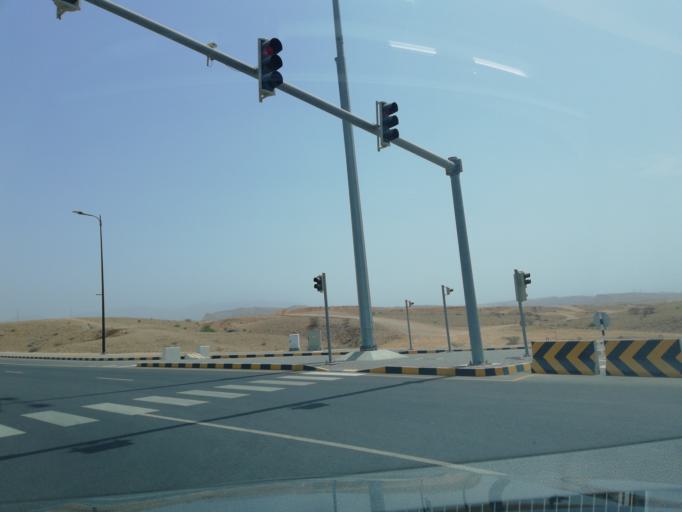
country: OM
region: Muhafazat Masqat
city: Bawshar
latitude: 23.5751
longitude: 58.3248
